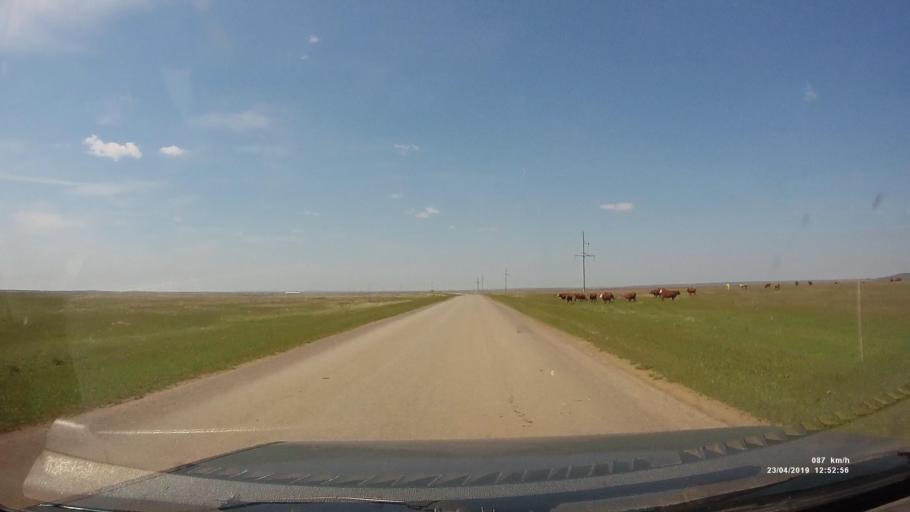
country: RU
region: Kalmykiya
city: Yashalta
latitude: 46.5694
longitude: 42.6030
